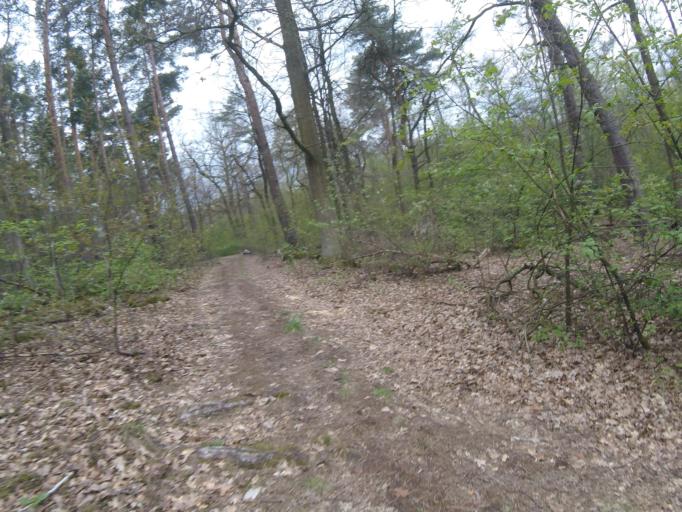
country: DE
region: Brandenburg
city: Bestensee
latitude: 52.2110
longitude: 13.6215
